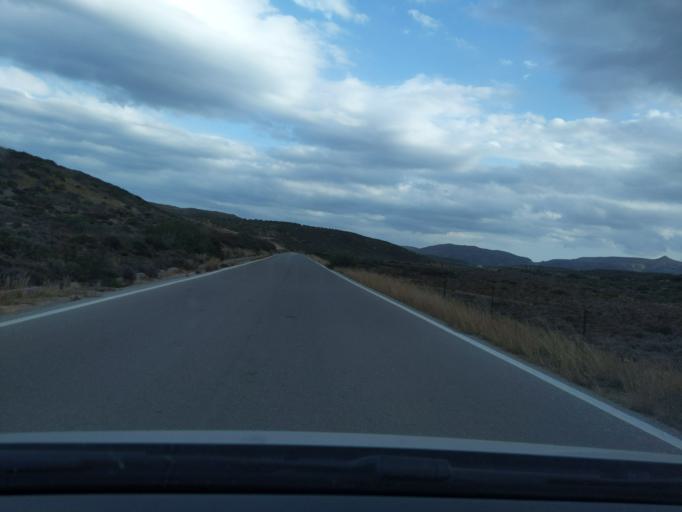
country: GR
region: Crete
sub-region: Nomos Lasithiou
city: Palekastro
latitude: 35.2377
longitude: 26.2492
